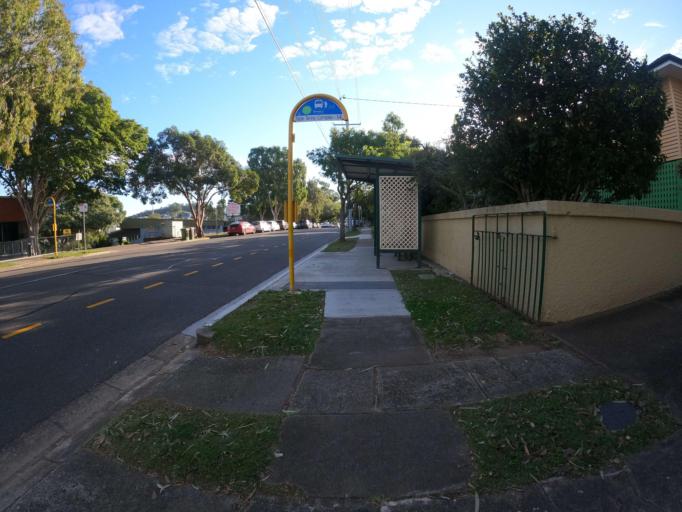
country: AU
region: Queensland
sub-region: Brisbane
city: Windsor
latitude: -27.4398
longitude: 153.0263
